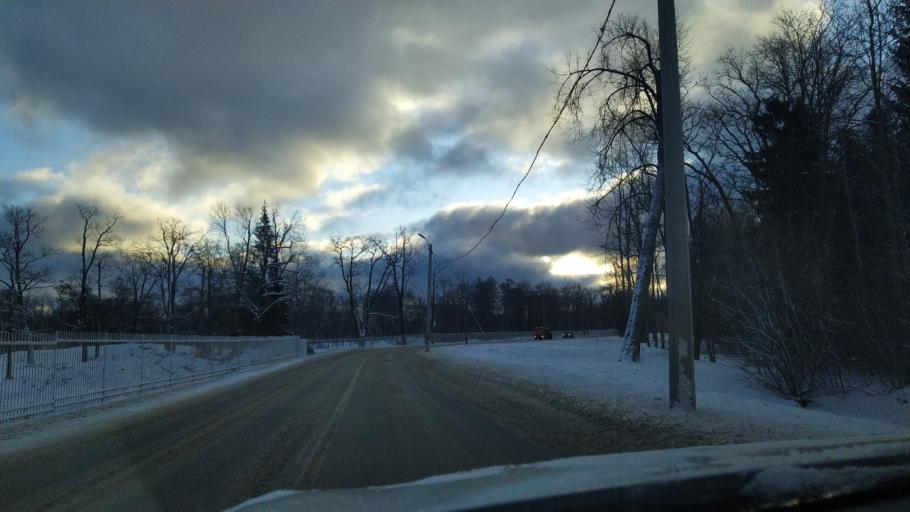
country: RU
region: St.-Petersburg
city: Pushkin
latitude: 59.7146
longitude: 30.3749
